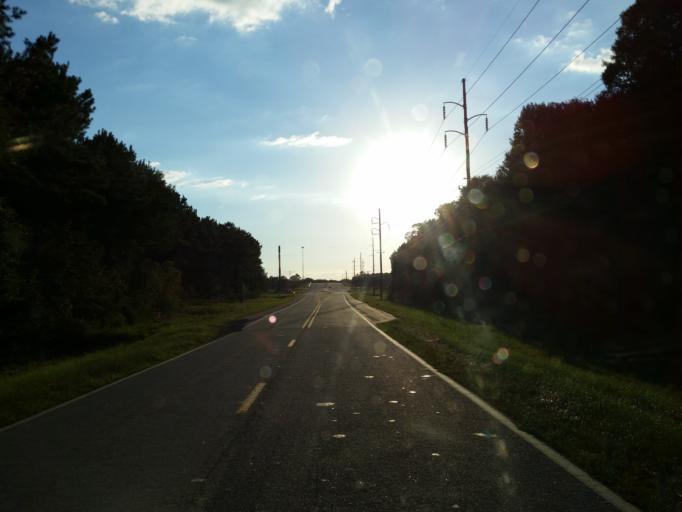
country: US
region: Georgia
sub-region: Crisp County
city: Cordele
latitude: 32.0056
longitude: -83.7518
